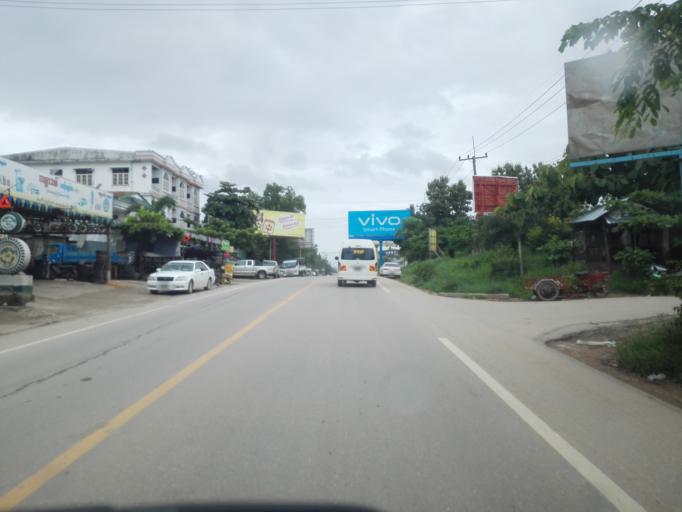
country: TH
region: Tak
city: Mae Sot
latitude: 16.6865
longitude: 98.4966
